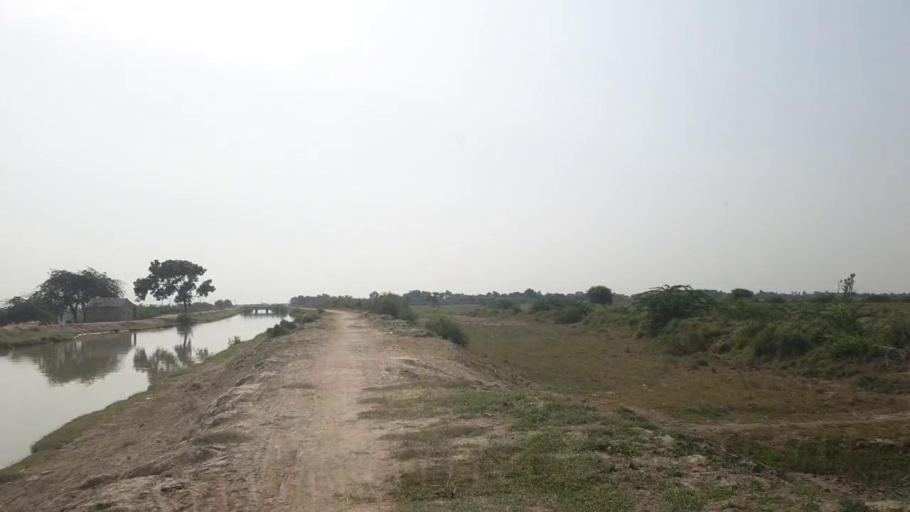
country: PK
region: Sindh
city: Badin
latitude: 24.5563
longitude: 68.8495
